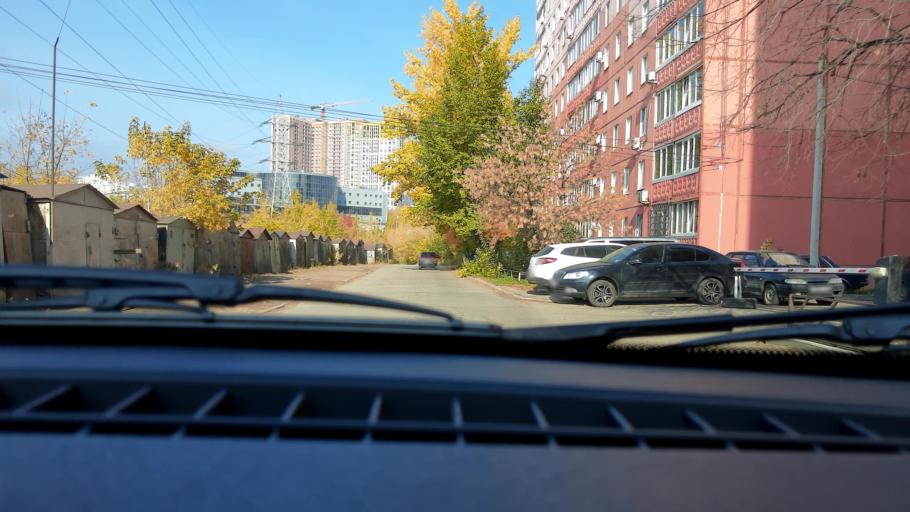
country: RU
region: Bashkortostan
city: Ufa
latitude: 54.7203
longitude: 55.9852
